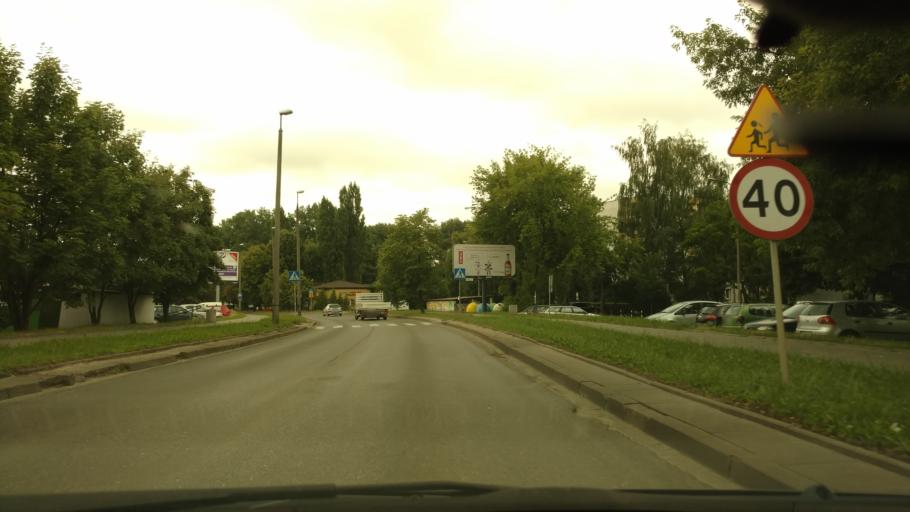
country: PL
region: Lesser Poland Voivodeship
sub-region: Krakow
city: Krakow
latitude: 50.0954
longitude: 19.9461
